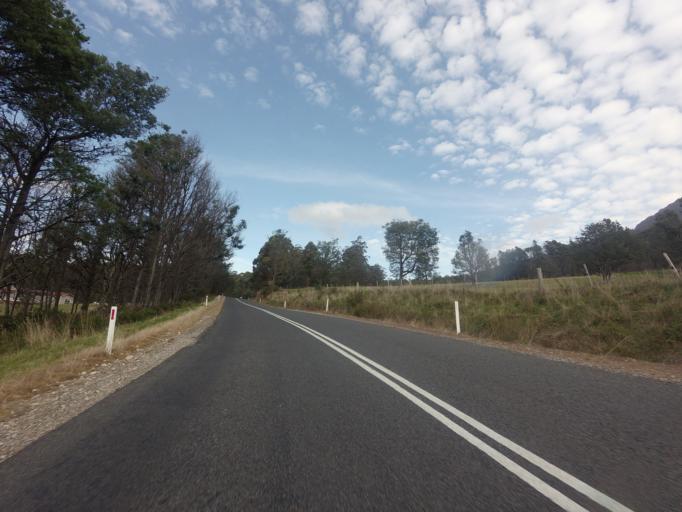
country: AU
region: Tasmania
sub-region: Meander Valley
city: Deloraine
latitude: -41.6357
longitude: 146.7130
